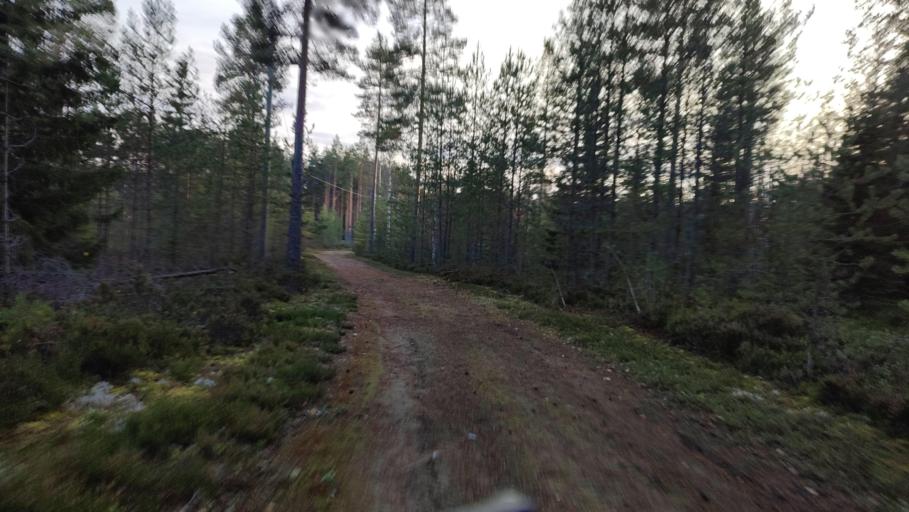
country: FI
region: Southern Ostrobothnia
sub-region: Suupohja
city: Karijoki
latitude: 62.2784
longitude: 21.6287
